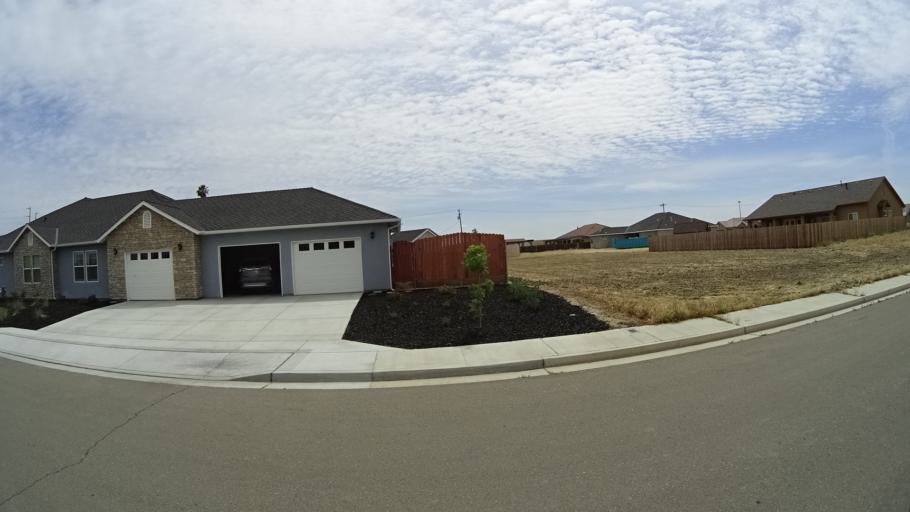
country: US
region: California
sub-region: Kings County
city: Lucerne
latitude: 36.3709
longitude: -119.6386
